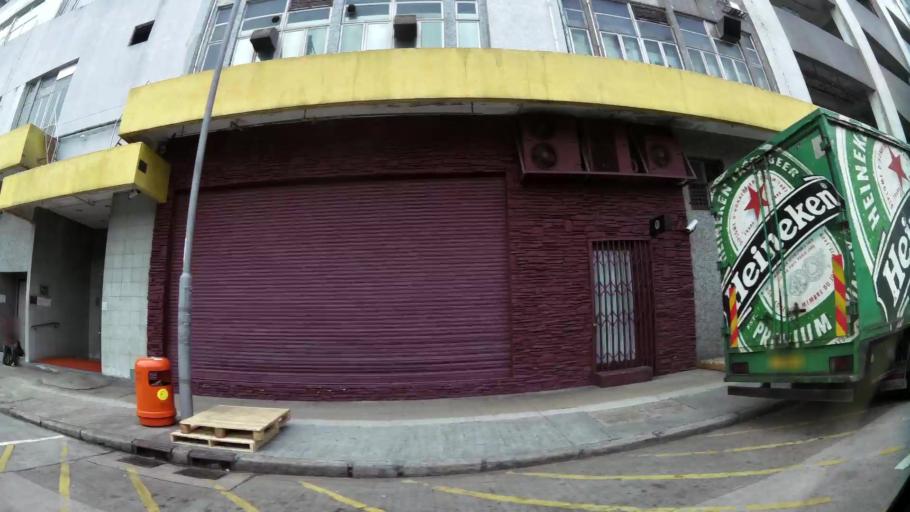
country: HK
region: Wanchai
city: Wan Chai
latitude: 22.2685
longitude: 114.2448
